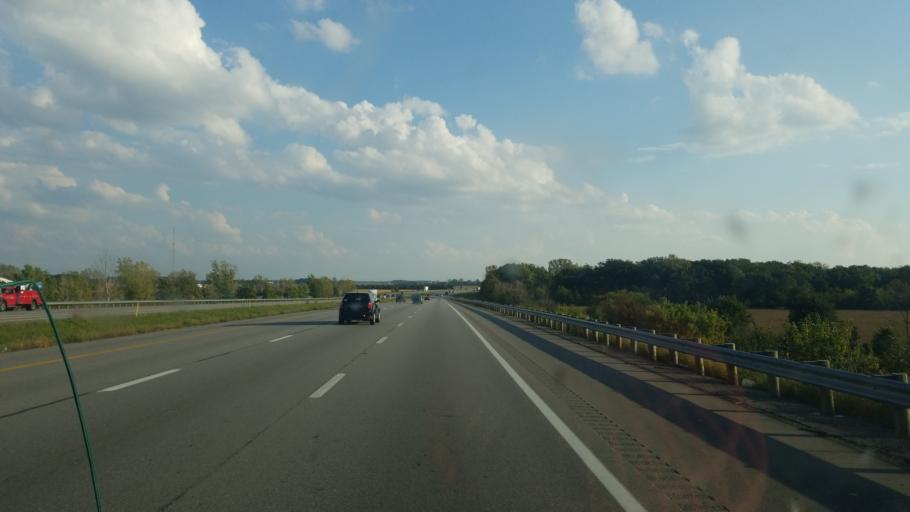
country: US
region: Ohio
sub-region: Wood County
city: Bowling Green
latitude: 41.4368
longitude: -83.6192
